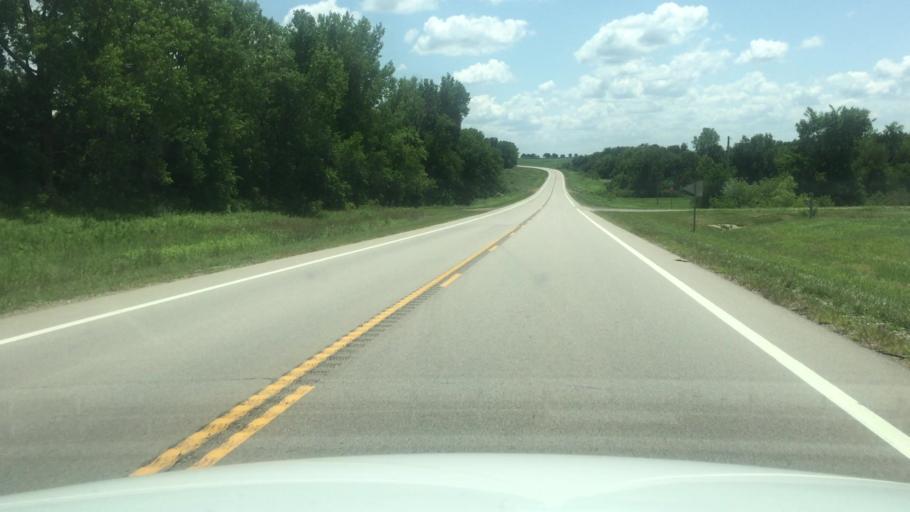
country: US
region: Kansas
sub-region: Brown County
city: Horton
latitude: 39.6246
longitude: -95.3503
